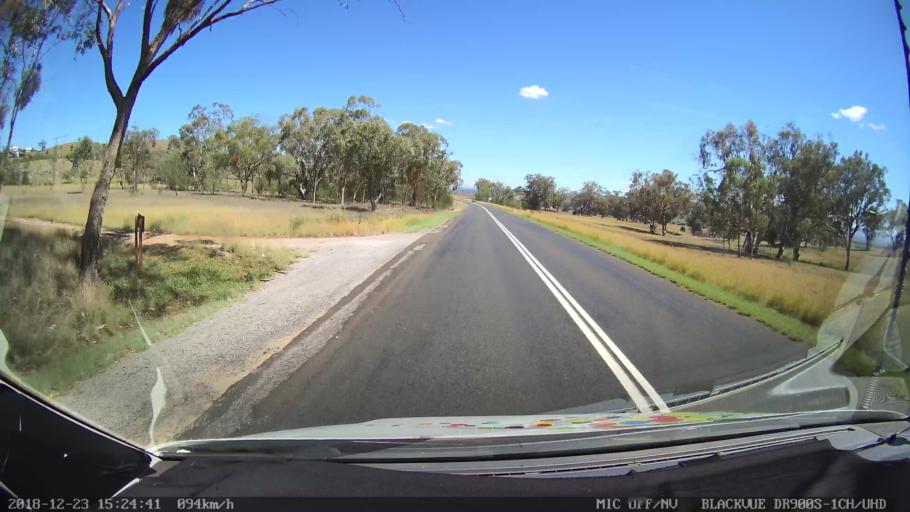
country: AU
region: New South Wales
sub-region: Tamworth Municipality
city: Manilla
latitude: -30.8949
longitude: 150.8246
